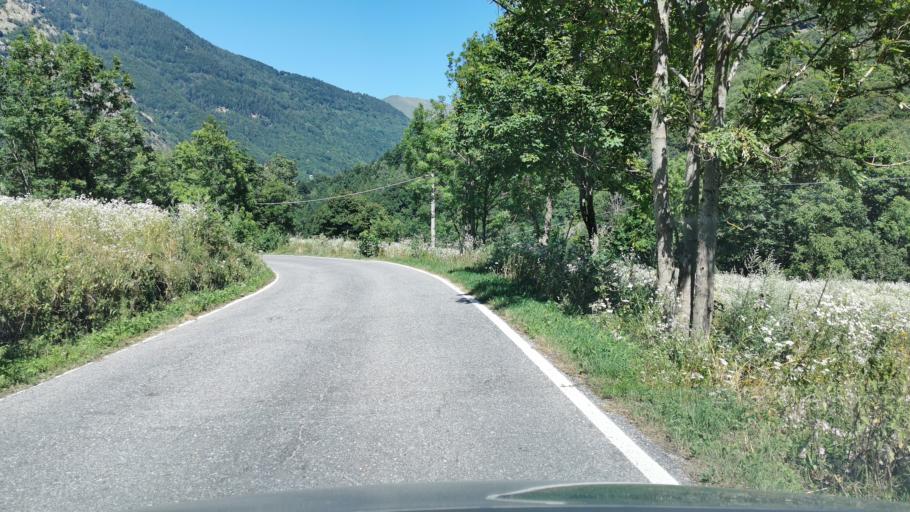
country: IT
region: Piedmont
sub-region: Provincia di Cuneo
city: Entracque
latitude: 44.2357
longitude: 7.3162
